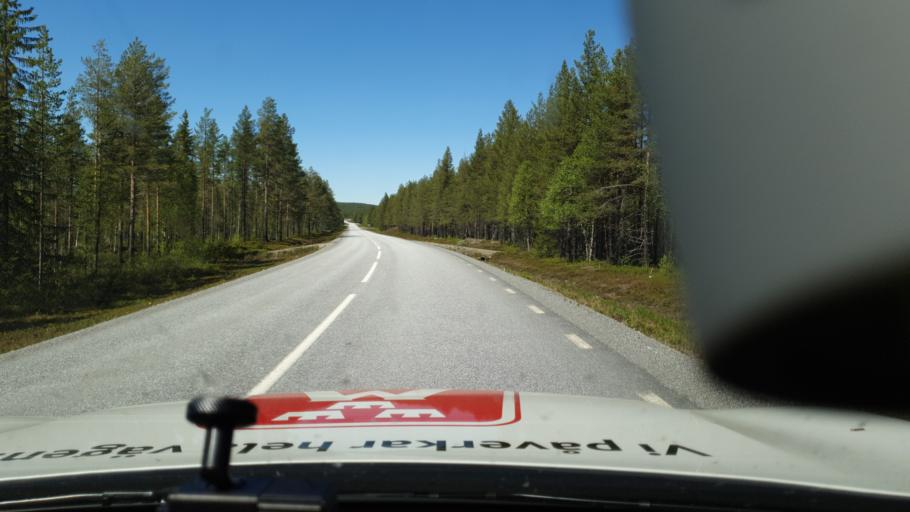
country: SE
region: Vaesterbotten
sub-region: Storumans Kommun
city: Storuman
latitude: 65.2220
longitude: 16.9720
